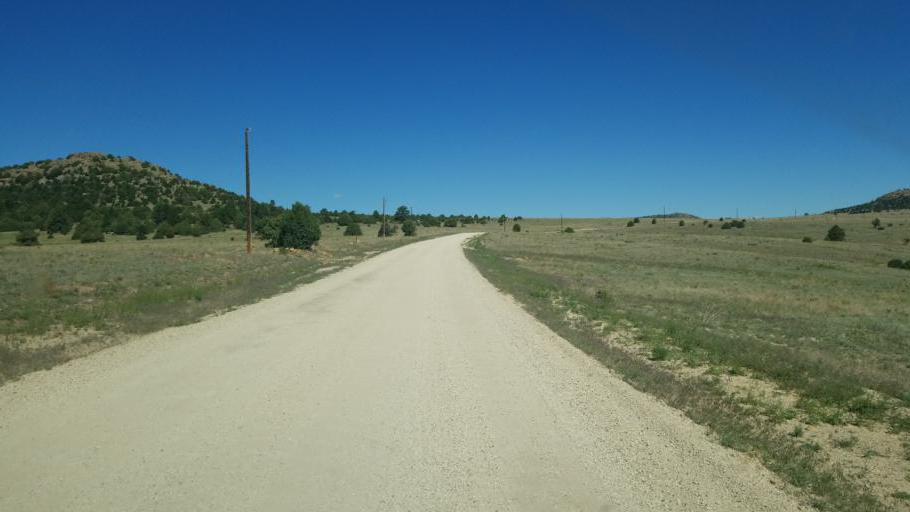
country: US
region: Colorado
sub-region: Custer County
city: Westcliffe
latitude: 38.2195
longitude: -105.4546
